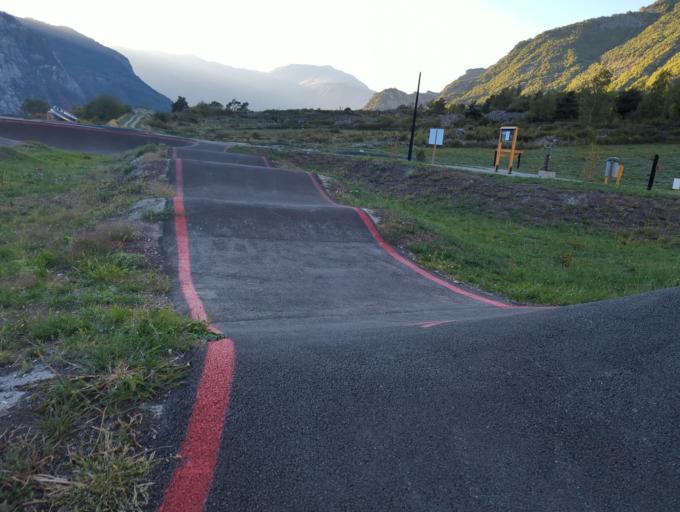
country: FR
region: Rhone-Alpes
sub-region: Departement de la Savoie
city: Saint-Michel-de-Maurienne
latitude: 45.2487
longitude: 6.4234
